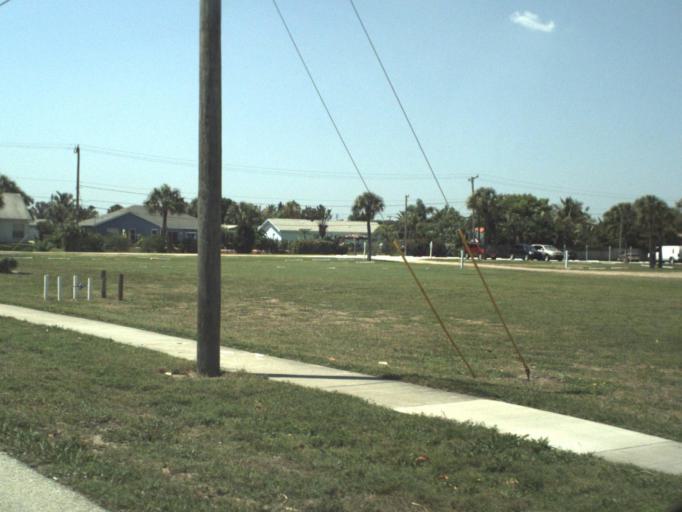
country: US
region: Florida
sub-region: Brevard County
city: Indialantic
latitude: 28.1186
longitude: -80.5757
